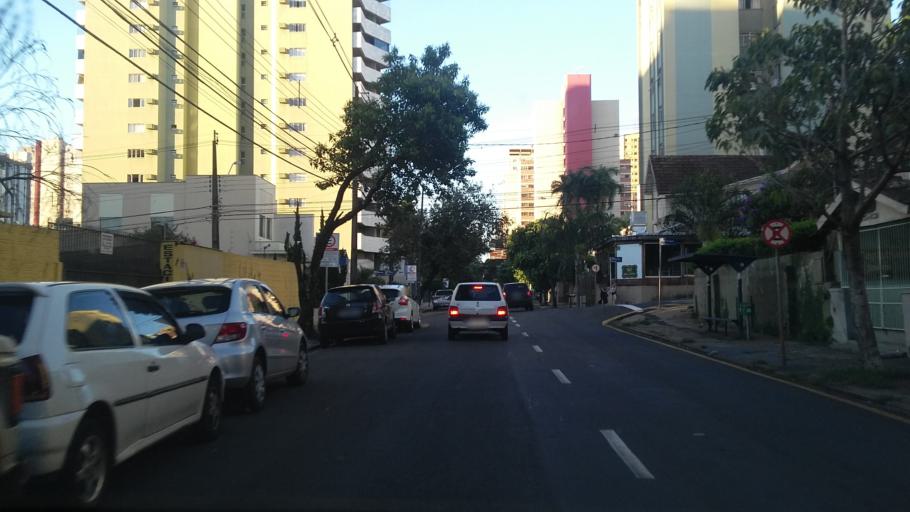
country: BR
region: Parana
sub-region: Londrina
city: Londrina
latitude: -23.3170
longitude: -51.1589
